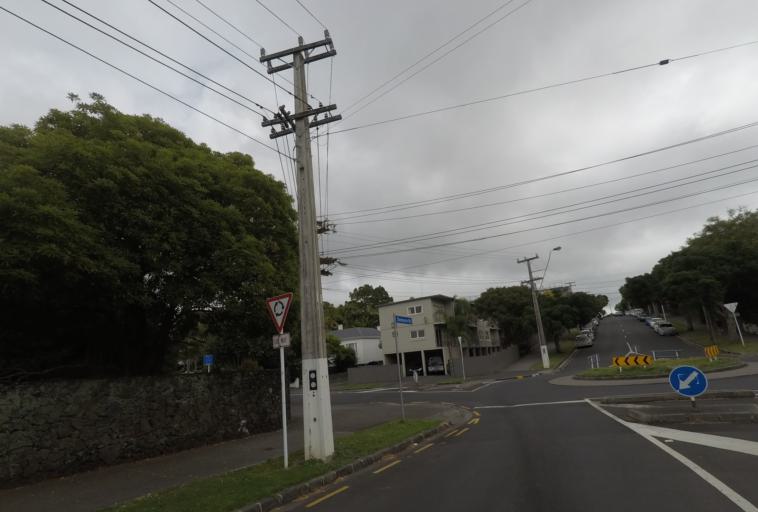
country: NZ
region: Auckland
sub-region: Auckland
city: Auckland
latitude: -36.8754
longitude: 174.7578
